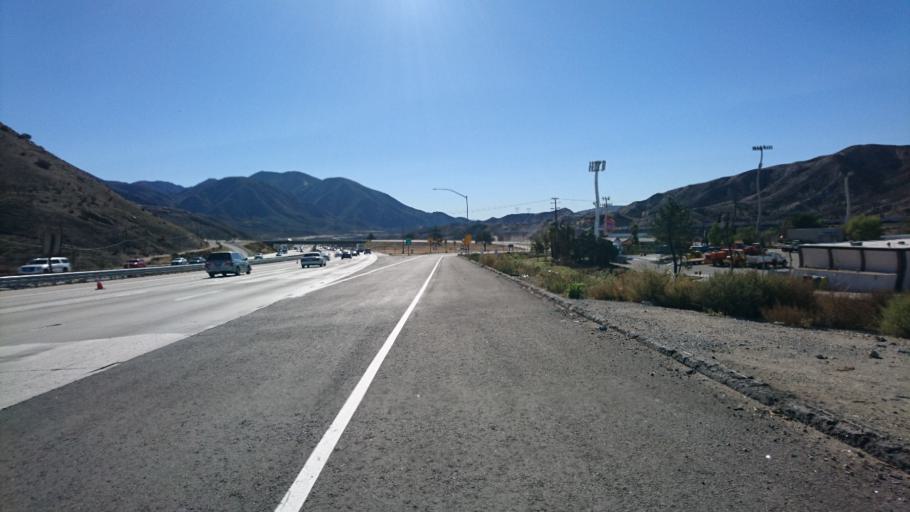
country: US
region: California
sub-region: San Bernardino County
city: Oak Hills
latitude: 34.3151
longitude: -117.4787
